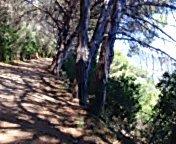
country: IT
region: Tuscany
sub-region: Provincia di Livorno
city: Capoliveri
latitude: 42.7490
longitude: 10.3192
